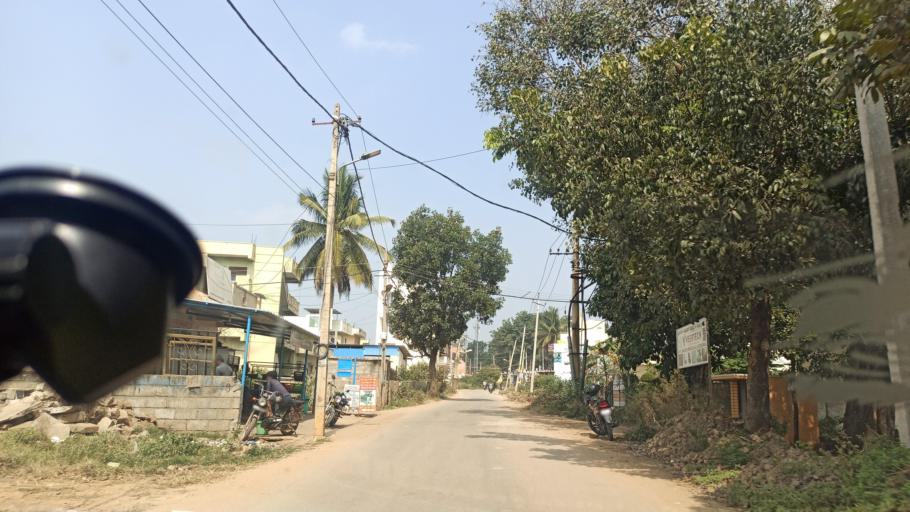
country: IN
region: Karnataka
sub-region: Bangalore Urban
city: Yelahanka
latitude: 13.0893
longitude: 77.6192
